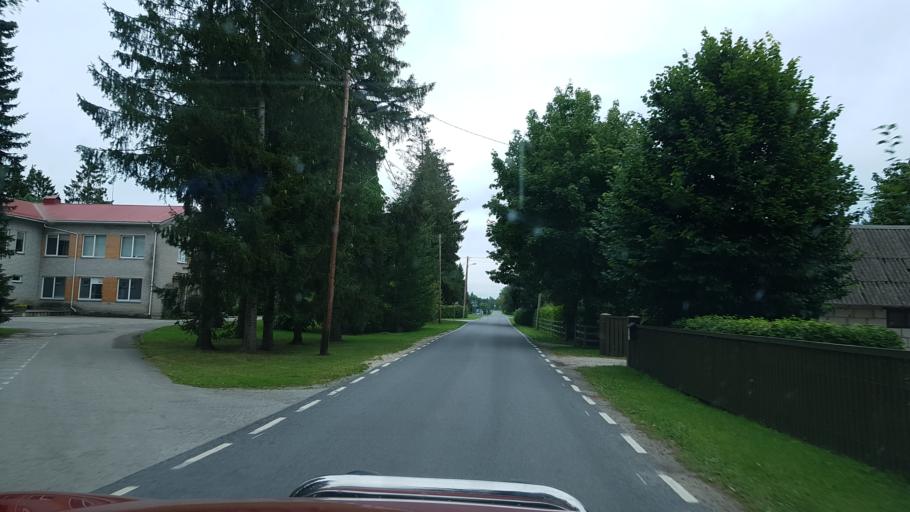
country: EE
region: Harju
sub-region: Nissi vald
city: Turba
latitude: 58.8797
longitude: 24.0767
